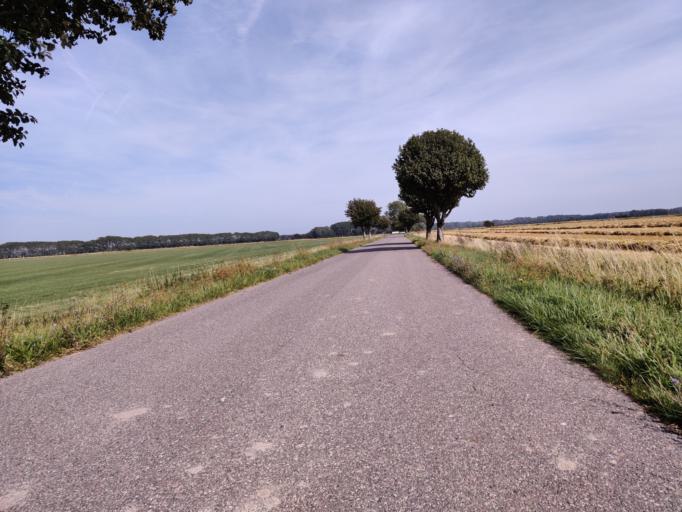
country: DK
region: Zealand
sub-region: Guldborgsund Kommune
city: Nykobing Falster
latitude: 54.6352
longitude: 11.9161
